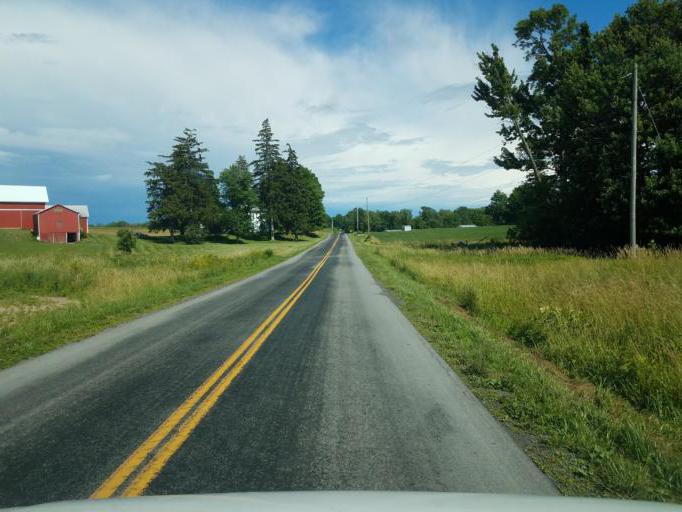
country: US
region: New York
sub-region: Wayne County
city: Clyde
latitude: 43.0129
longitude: -76.8706
